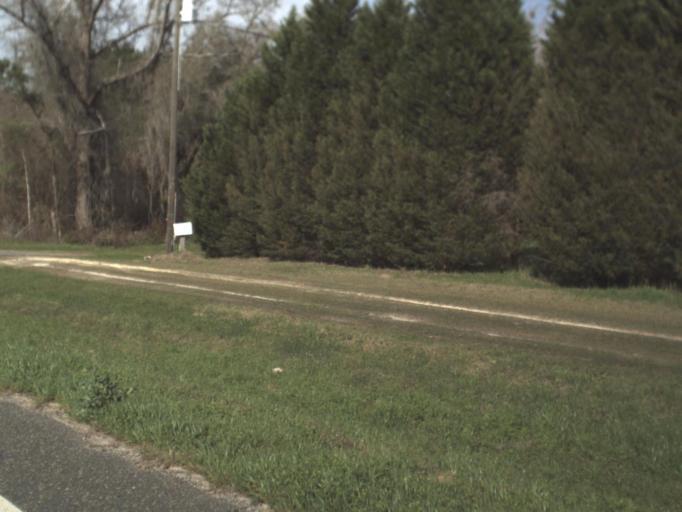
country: US
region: Florida
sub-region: Jefferson County
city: Monticello
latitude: 30.4649
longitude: -83.8919
